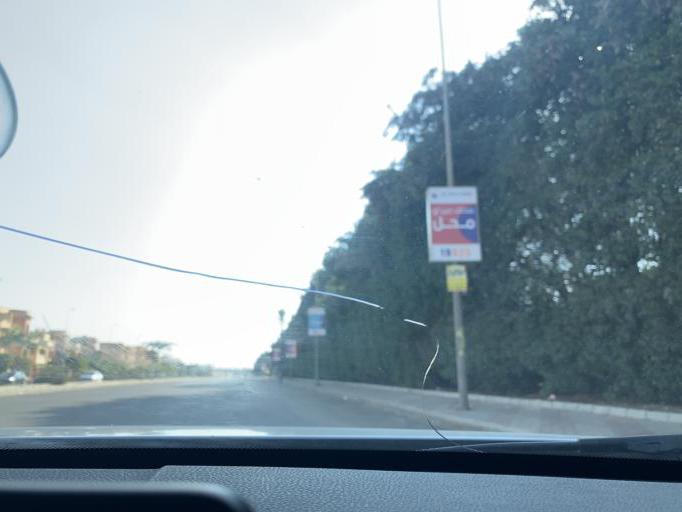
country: EG
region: Muhafazat al Qalyubiyah
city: Al Khankah
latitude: 30.0182
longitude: 31.4859
